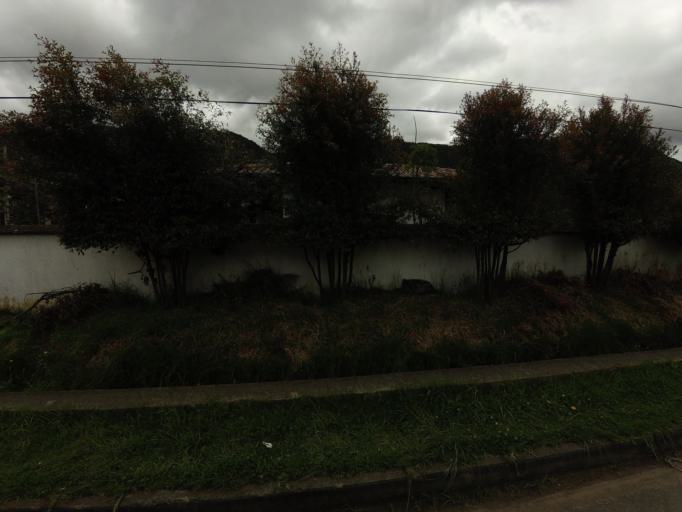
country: CO
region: Cundinamarca
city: Cajica
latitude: 4.9316
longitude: -74.0467
